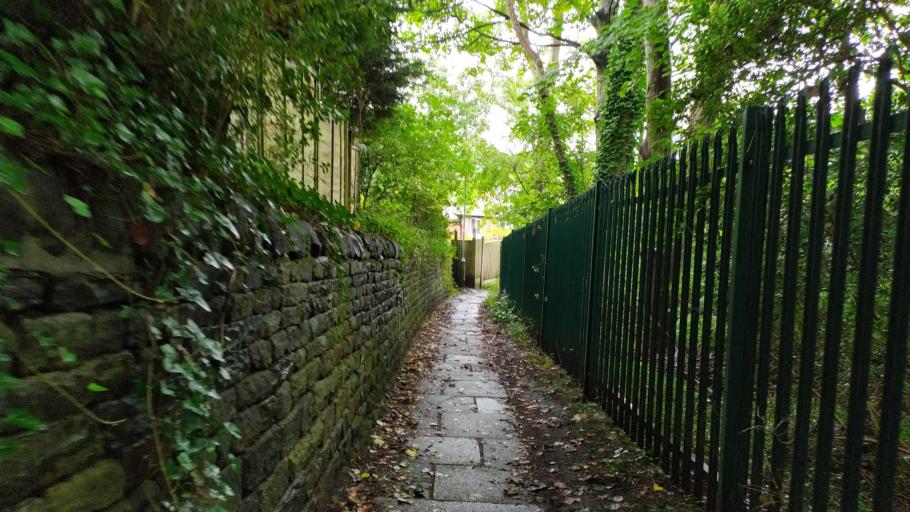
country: GB
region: England
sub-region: City and Borough of Leeds
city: Chapel Allerton
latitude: 53.8284
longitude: -1.5749
